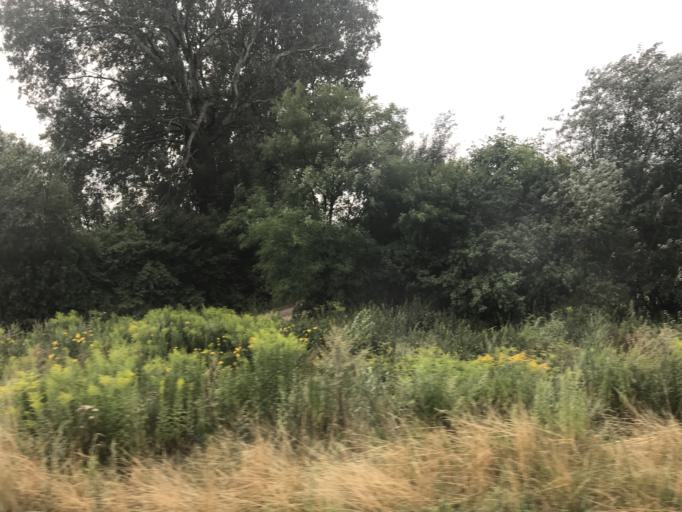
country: PL
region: Greater Poland Voivodeship
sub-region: Powiat gnieznienski
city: Niechanowo
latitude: 52.5331
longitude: 17.6574
